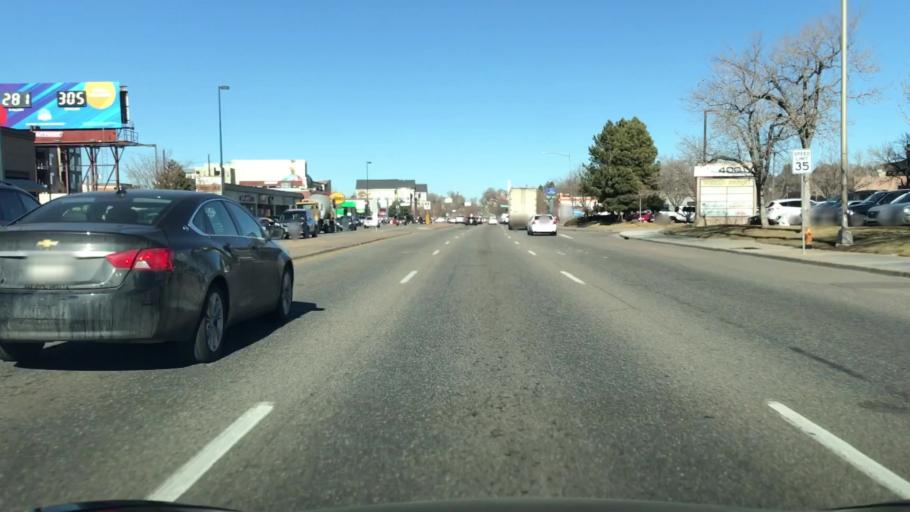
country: US
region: Colorado
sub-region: Arapahoe County
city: Glendale
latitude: 39.7091
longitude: -104.9407
